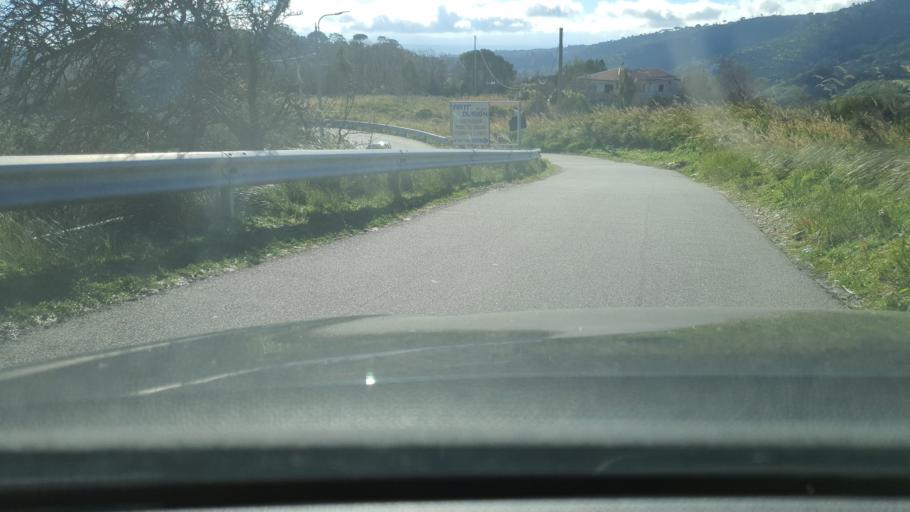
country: IT
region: Calabria
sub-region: Provincia di Catanzaro
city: Sant'Elia
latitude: 38.9504
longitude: 16.5818
